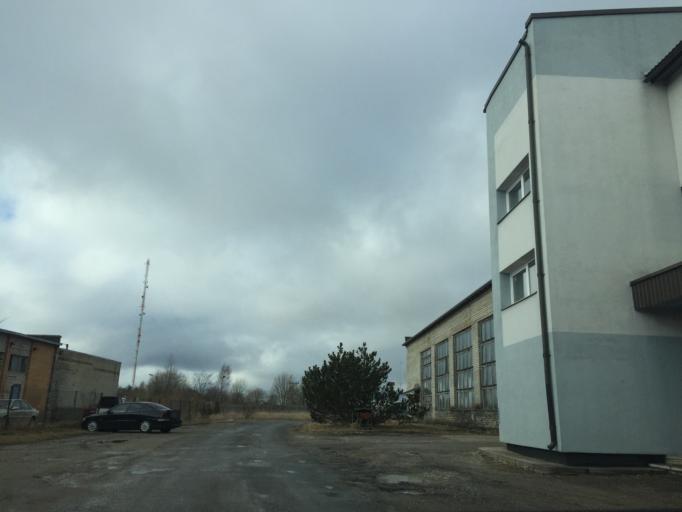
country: EE
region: Laeaene
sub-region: Haapsalu linn
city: Haapsalu
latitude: 58.9580
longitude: 23.5238
